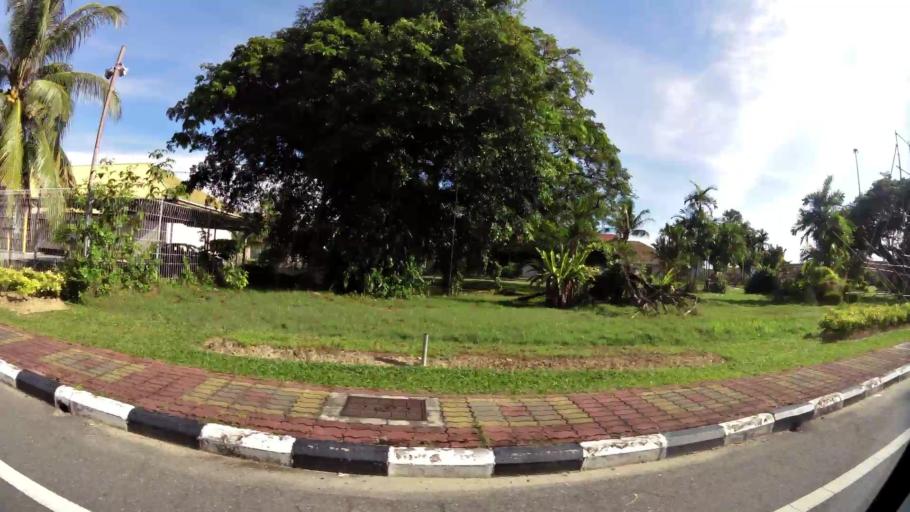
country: BN
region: Belait
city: Kuala Belait
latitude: 4.5885
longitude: 114.1918
